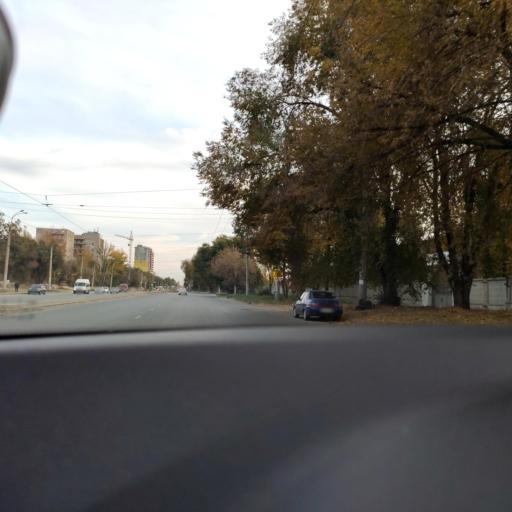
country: RU
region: Samara
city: Smyshlyayevka
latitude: 53.2066
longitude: 50.2780
